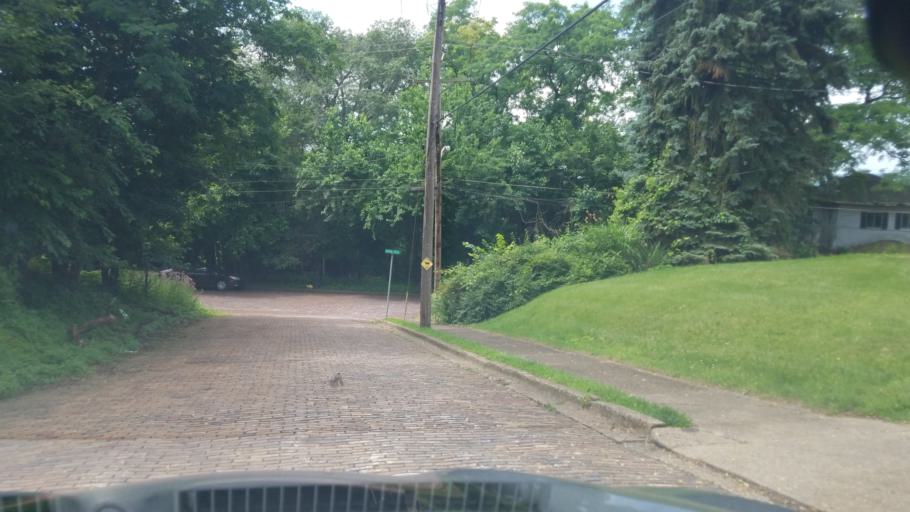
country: US
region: Pennsylvania
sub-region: Allegheny County
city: Swissvale
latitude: 40.4190
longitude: -79.8796
